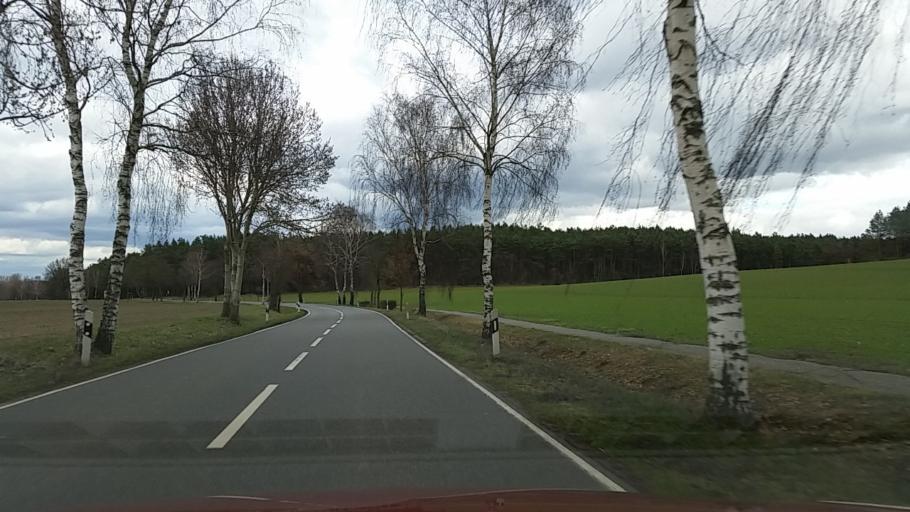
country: DE
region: Lower Saxony
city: Karwitz
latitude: 53.1181
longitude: 10.9508
